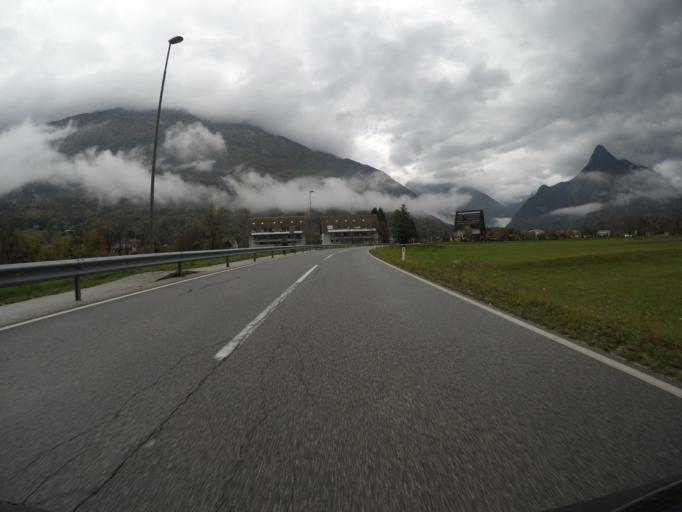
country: SI
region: Bovec
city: Bovec
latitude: 46.3365
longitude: 13.5587
